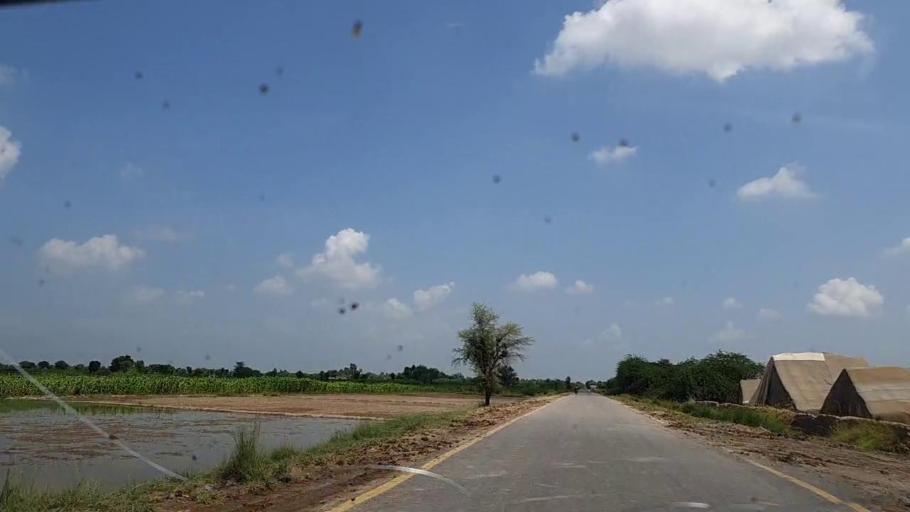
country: PK
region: Sindh
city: Tharu Shah
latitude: 26.9719
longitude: 68.0903
